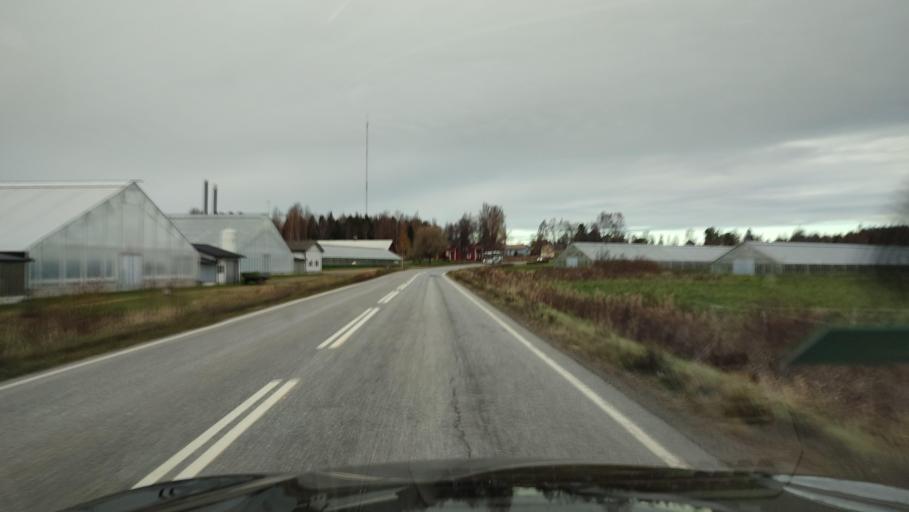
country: FI
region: Ostrobothnia
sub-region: Sydosterbotten
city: Naerpes
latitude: 62.4050
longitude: 21.3521
